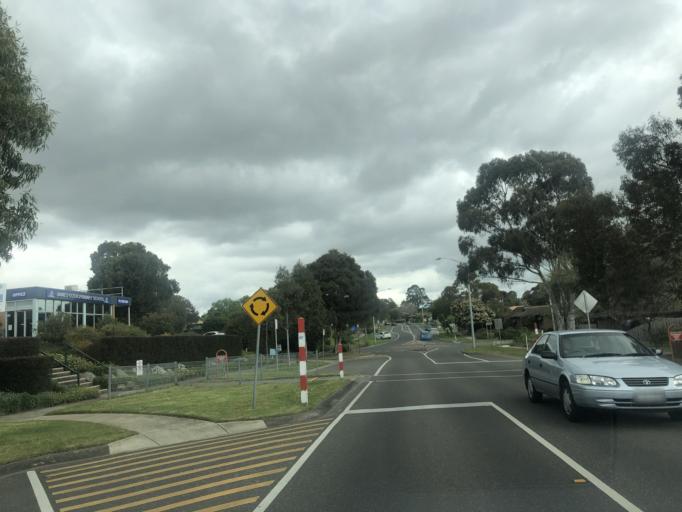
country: AU
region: Victoria
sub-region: Casey
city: Endeavour Hills
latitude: -37.9785
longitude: 145.2456
